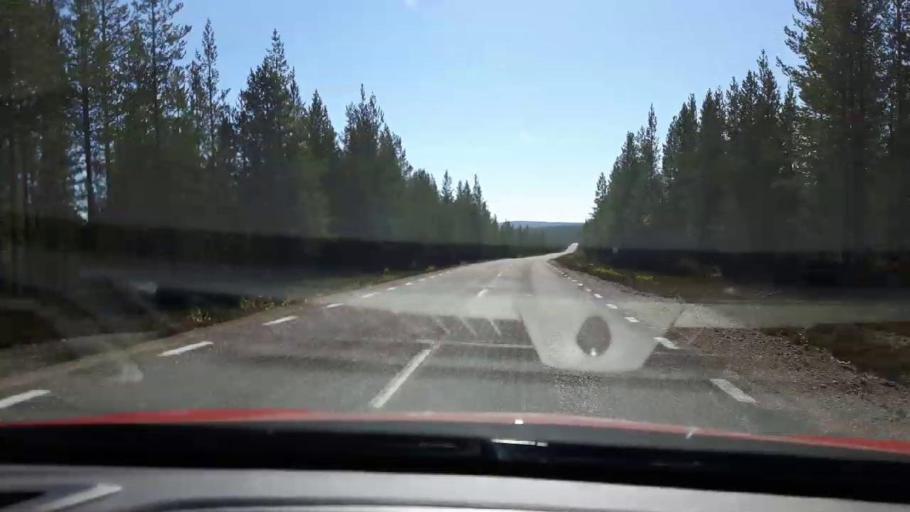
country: SE
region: Jaemtland
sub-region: Harjedalens Kommun
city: Sveg
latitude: 61.7212
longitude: 14.1677
